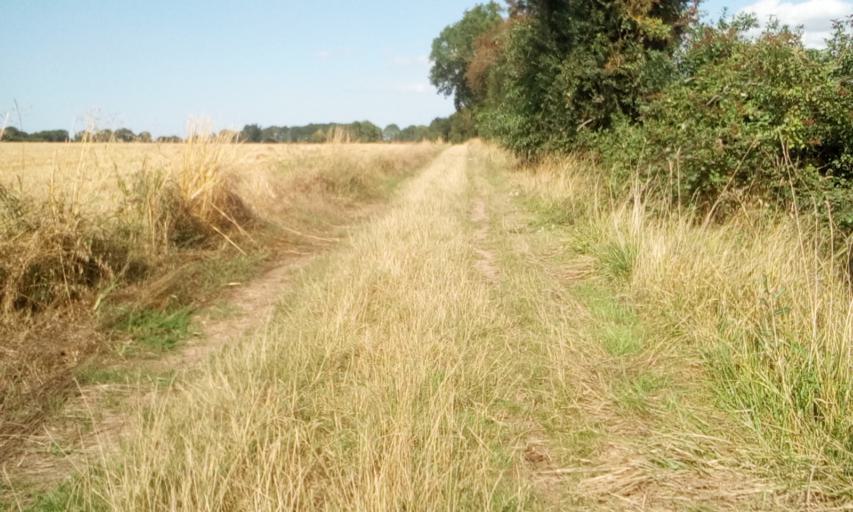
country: FR
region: Lower Normandy
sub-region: Departement du Calvados
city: Argences
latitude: 49.1354
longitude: -0.1144
